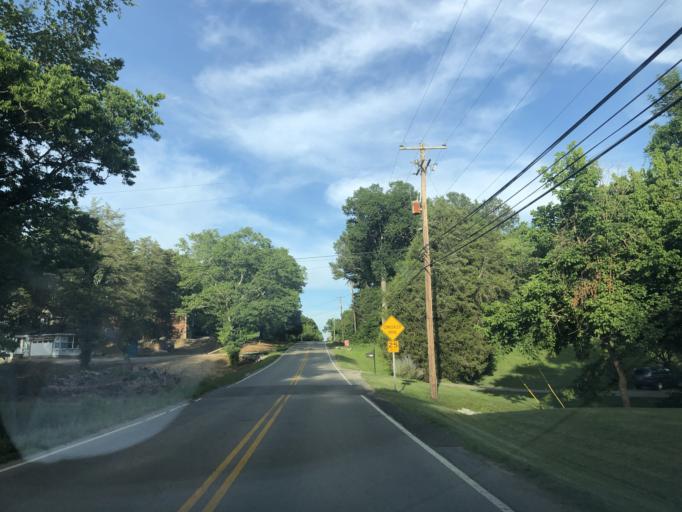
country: US
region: Tennessee
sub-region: Davidson County
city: Belle Meade
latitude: 36.0630
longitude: -86.9313
